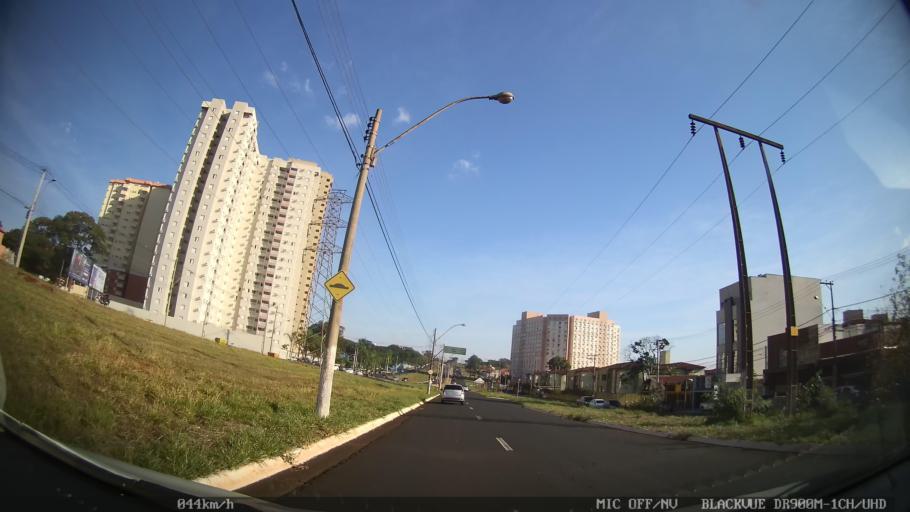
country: BR
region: Sao Paulo
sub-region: Ribeirao Preto
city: Ribeirao Preto
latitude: -21.1961
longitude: -47.7783
